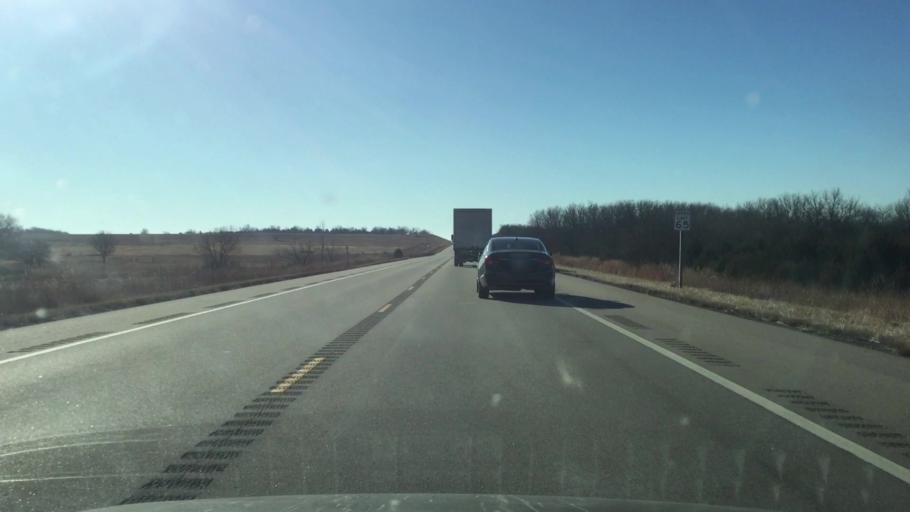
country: US
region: Kansas
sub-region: Allen County
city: Iola
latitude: 38.0220
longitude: -95.3807
